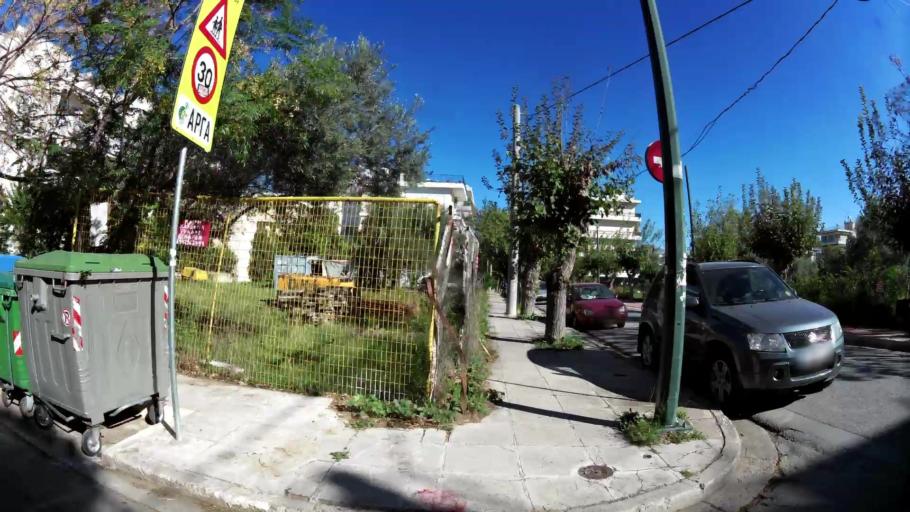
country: GR
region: Attica
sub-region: Nomarchia Athinas
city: Khalandrion
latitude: 38.0208
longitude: 23.8097
